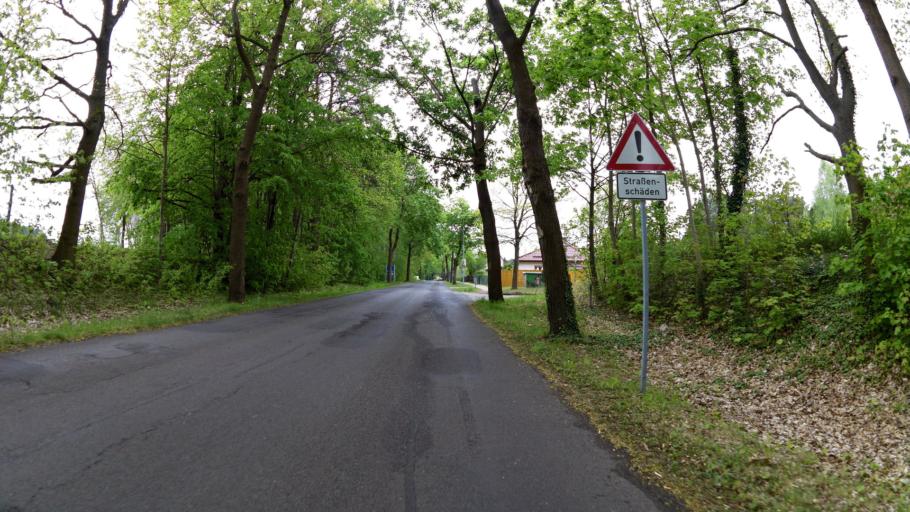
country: DE
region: Brandenburg
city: Bestensee
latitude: 52.2126
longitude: 13.5957
